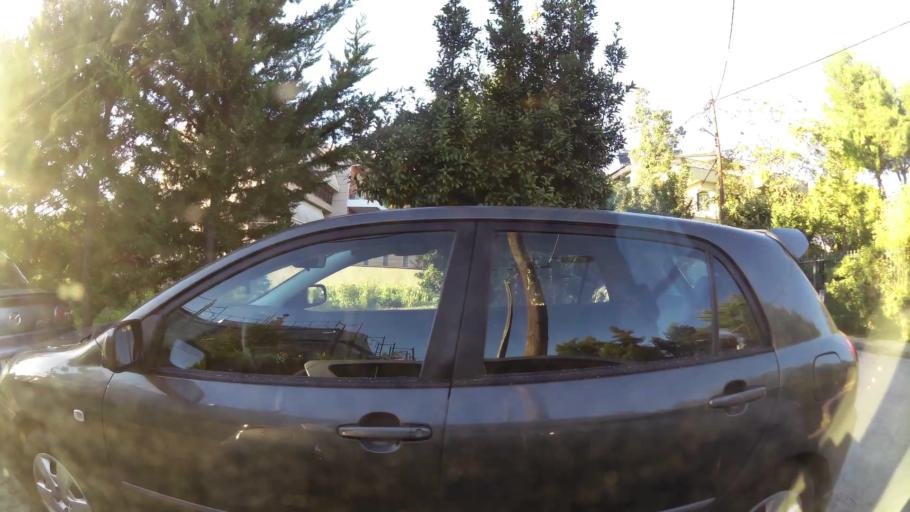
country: GR
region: Attica
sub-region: Nomarchia Anatolikis Attikis
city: Kryoneri
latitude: 38.1378
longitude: 23.8265
